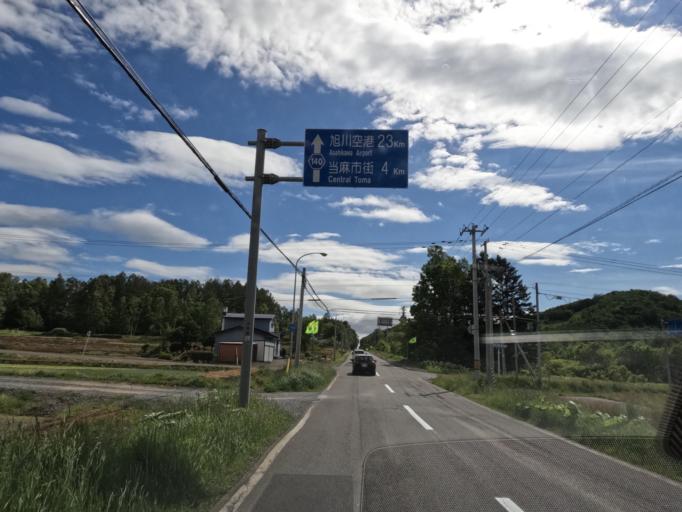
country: JP
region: Hokkaido
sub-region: Asahikawa-shi
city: Asahikawa
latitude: 43.8392
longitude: 142.5432
